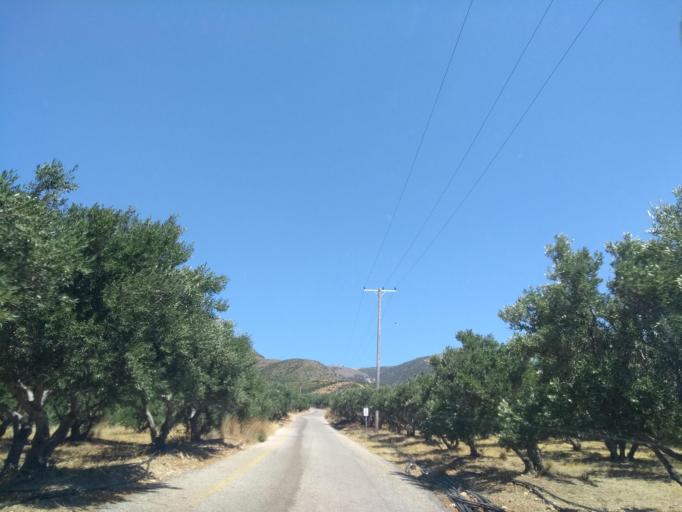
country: GR
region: Crete
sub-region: Nomos Chanias
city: Vryses
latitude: 35.3615
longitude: 23.5377
